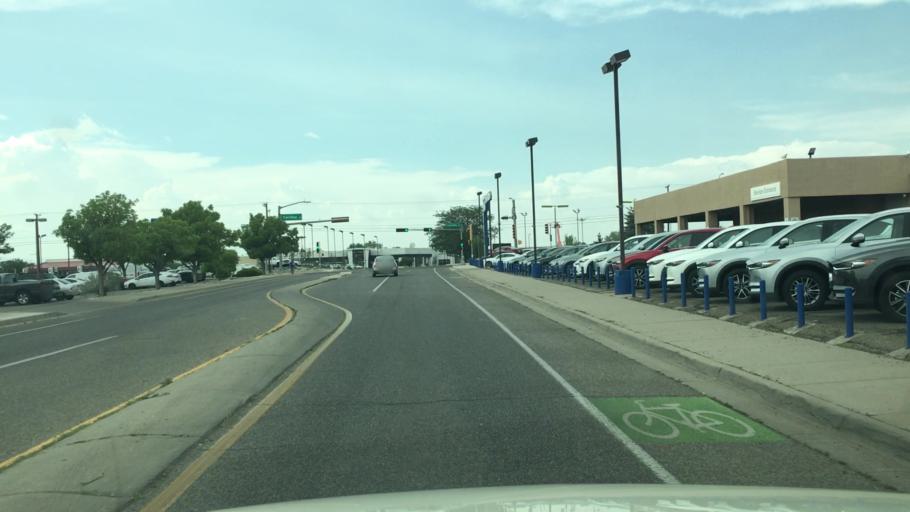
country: US
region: New Mexico
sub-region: Santa Fe County
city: Agua Fria
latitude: 35.6572
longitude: -105.9855
